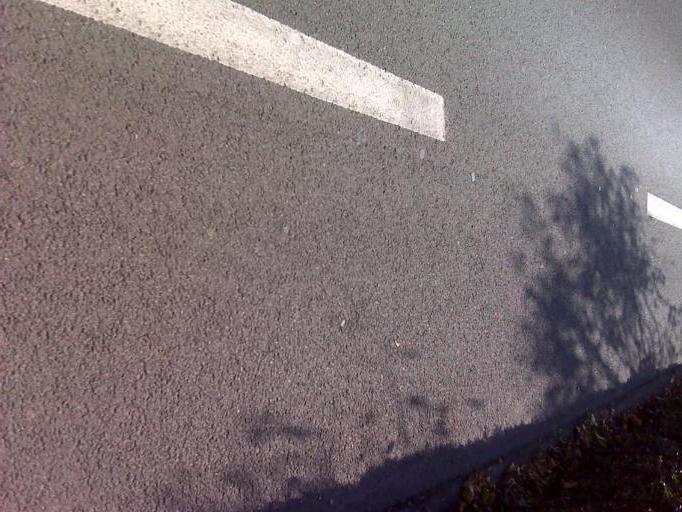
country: FR
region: Poitou-Charentes
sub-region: Departement de la Charente-Maritime
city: Rochefort
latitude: 45.9408
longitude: -0.9871
